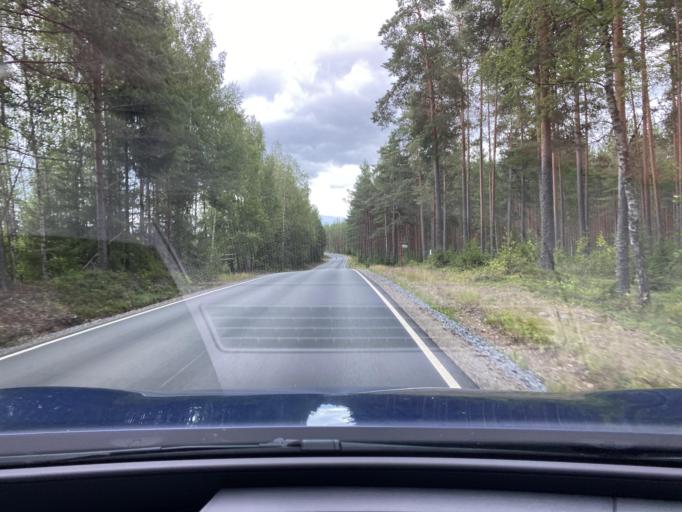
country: FI
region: Pirkanmaa
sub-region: Lounais-Pirkanmaa
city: Vammala
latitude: 61.2878
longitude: 23.0143
